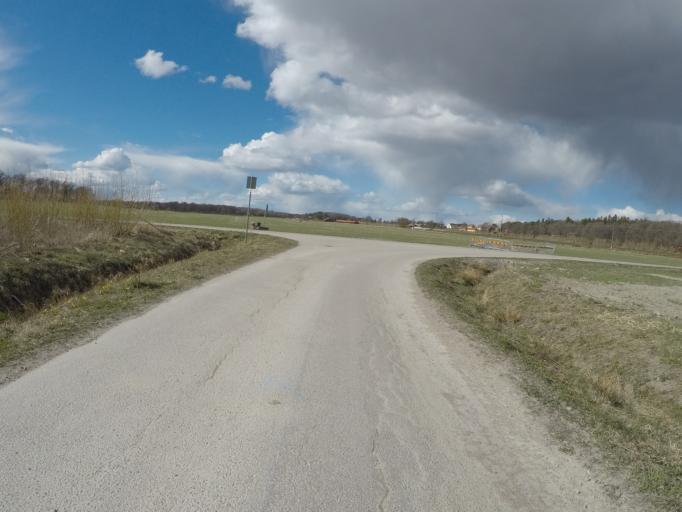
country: SE
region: Vaestmanland
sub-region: Hallstahammars Kommun
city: Kolback
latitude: 59.5119
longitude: 16.2545
